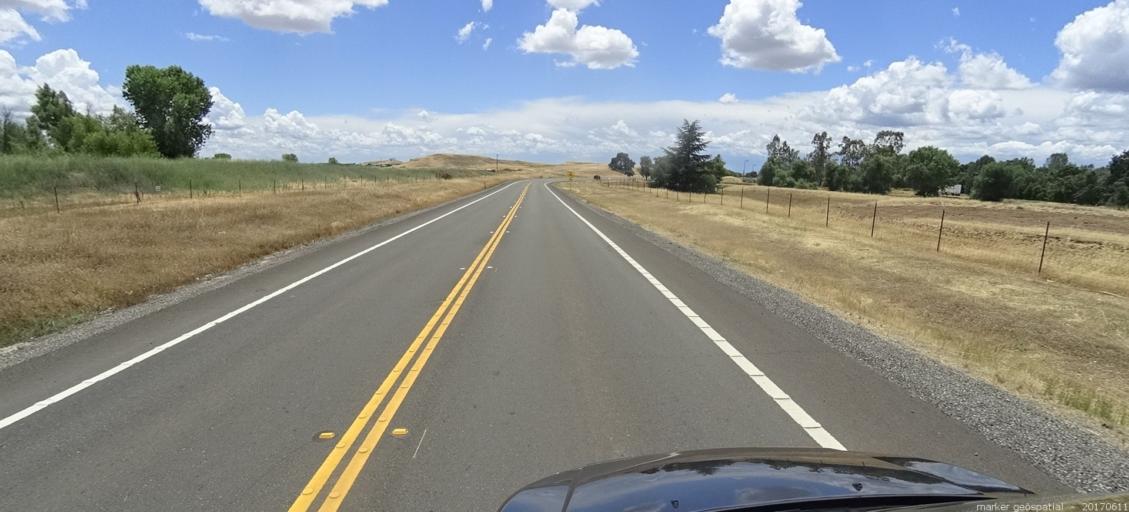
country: US
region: California
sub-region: Butte County
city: Paradise
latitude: 39.6452
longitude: -121.6393
